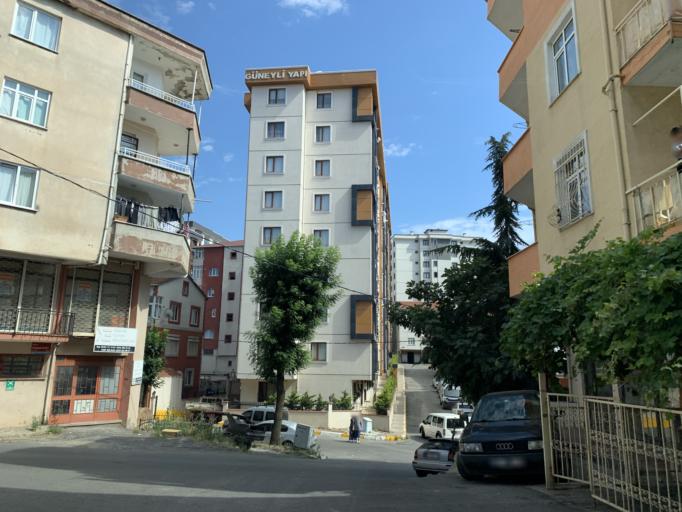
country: TR
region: Istanbul
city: Pendik
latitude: 40.8948
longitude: 29.2519
